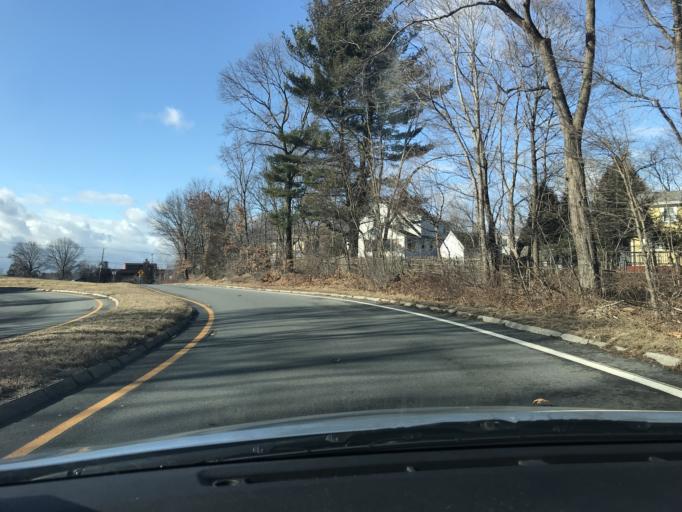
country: US
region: Massachusetts
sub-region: Middlesex County
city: Lexington
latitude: 42.4721
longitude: -71.2443
